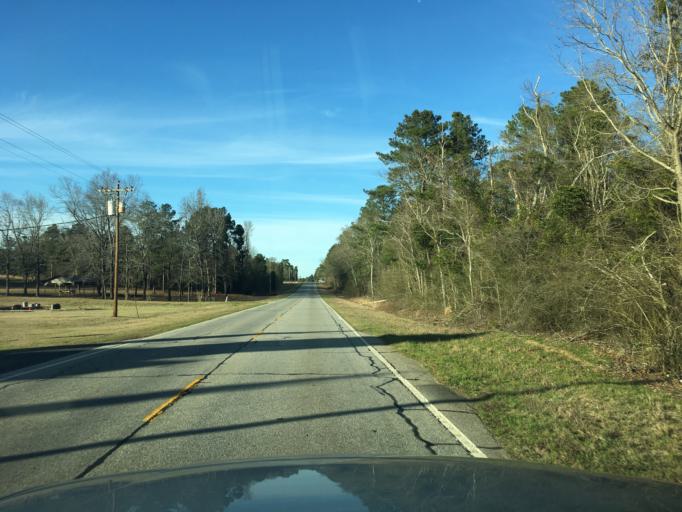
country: US
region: South Carolina
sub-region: Lexington County
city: Batesburg
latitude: 33.7630
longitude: -81.6420
